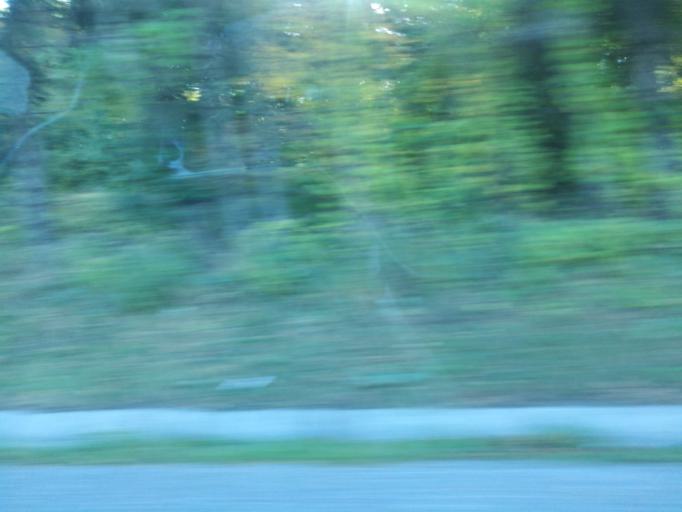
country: RO
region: Brasov
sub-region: Comuna Dumbravita
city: Dumbravita
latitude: 45.7608
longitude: 25.3841
